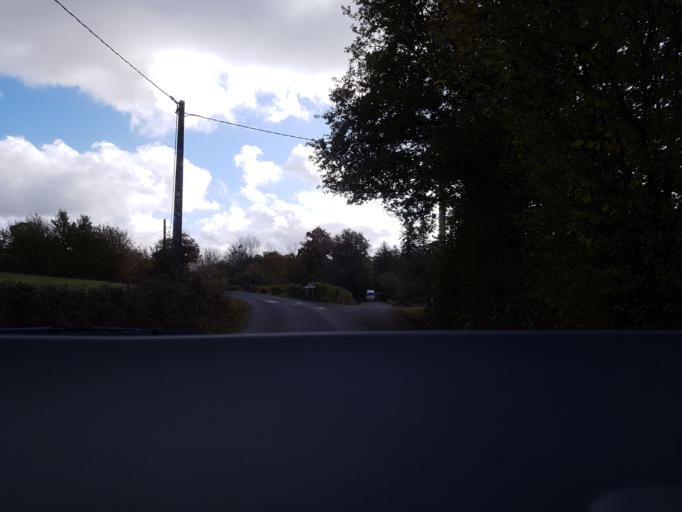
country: FR
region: Lower Normandy
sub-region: Departement de l'Orne
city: Champsecret
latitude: 48.6379
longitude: -0.5824
